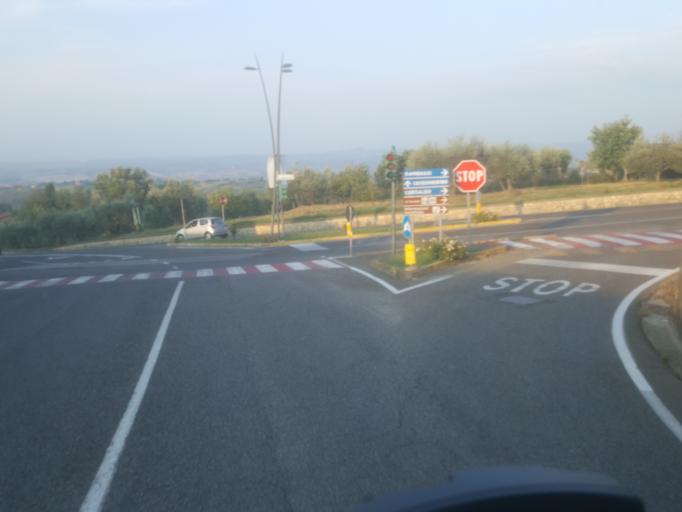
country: IT
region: Tuscany
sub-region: Province of Florence
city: Gambassi Terme
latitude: 43.5421
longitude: 10.9548
